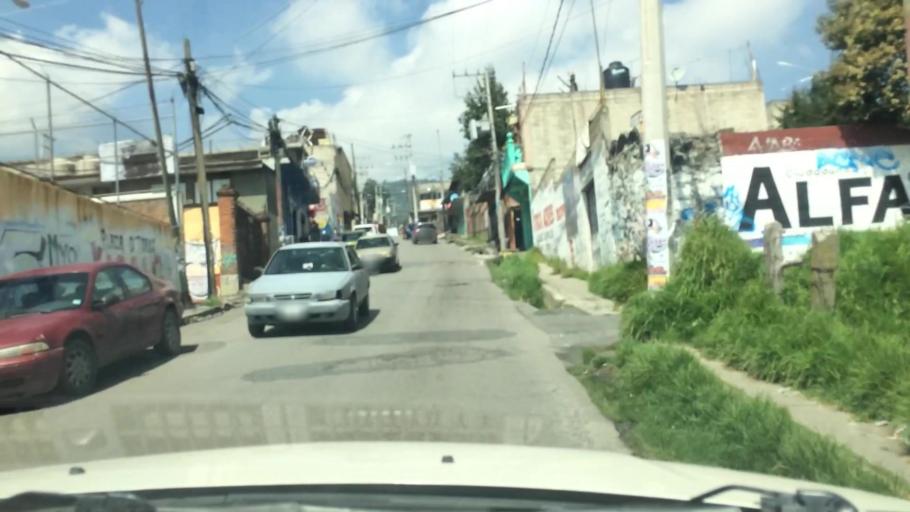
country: MX
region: Mexico City
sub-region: Tlalpan
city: Lomas de Tepemecatl
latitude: 19.2265
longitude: -99.2010
